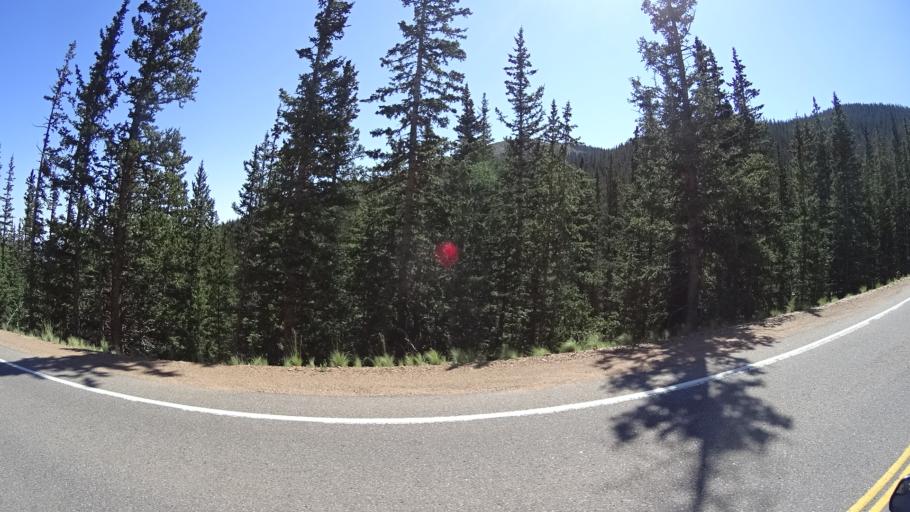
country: US
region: Colorado
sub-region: El Paso County
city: Cascade-Chipita Park
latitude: 38.8831
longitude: -105.0715
